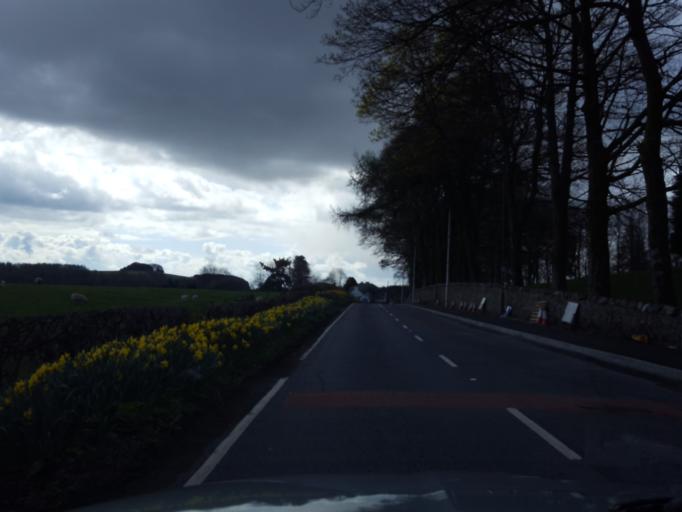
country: GB
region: Scotland
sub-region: Clackmannanshire
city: Dollar
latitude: 56.1923
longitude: -3.6078
